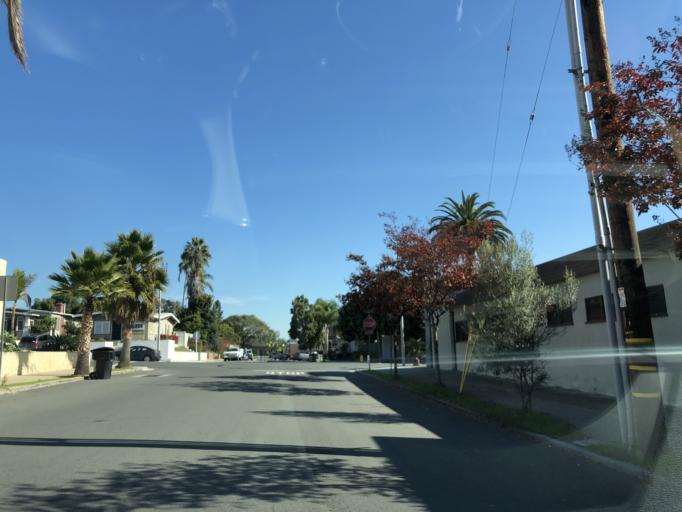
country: US
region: California
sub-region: San Diego County
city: San Diego
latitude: 32.7234
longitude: -117.1308
